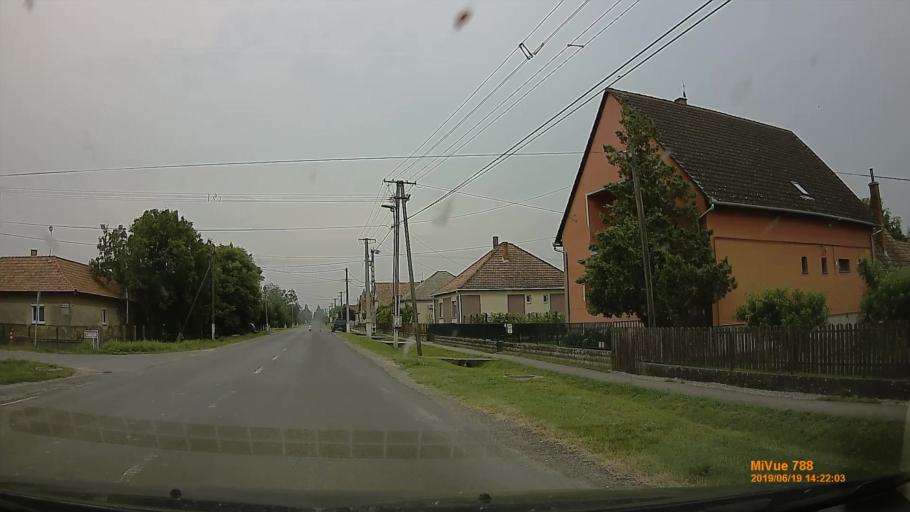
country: HU
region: Baranya
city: Szigetvar
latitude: 46.0160
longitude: 17.7683
